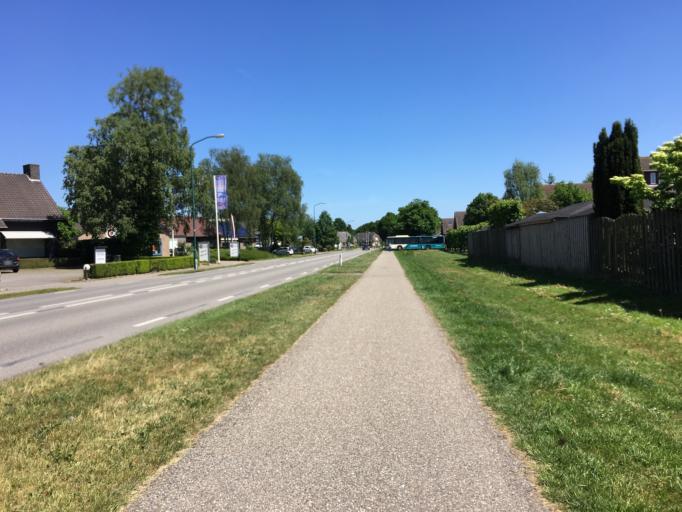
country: NL
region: Gelderland
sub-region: Gemeente Zaltbommel
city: Nederhemert-Noord
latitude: 51.7503
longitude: 5.2145
